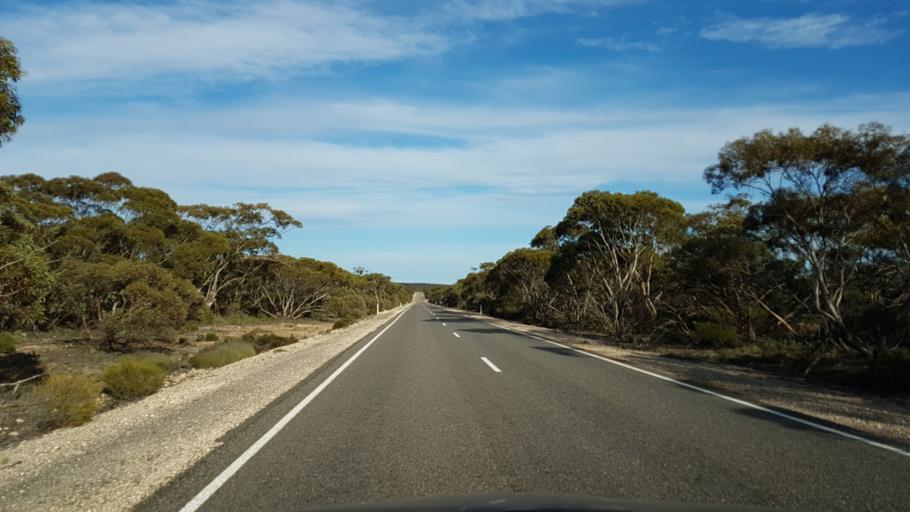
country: AU
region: South Australia
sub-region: Mid Murray
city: Mannum
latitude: -35.0038
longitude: 139.5419
